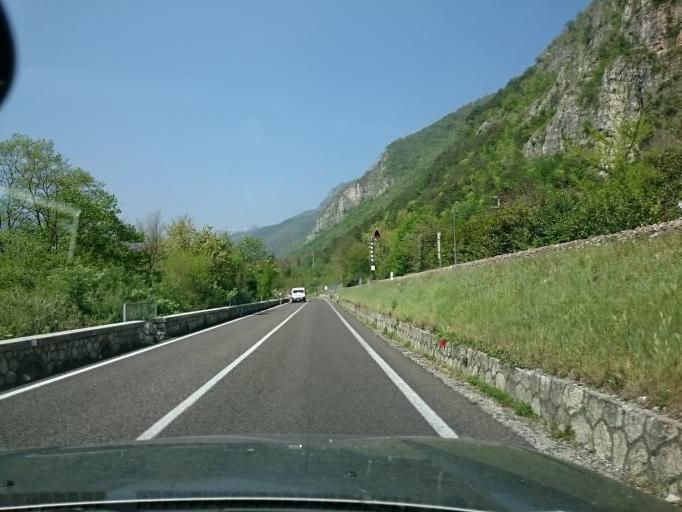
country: IT
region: Veneto
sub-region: Provincia di Vicenza
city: Campolongo sul Brenta
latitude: 45.8298
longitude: 11.7029
